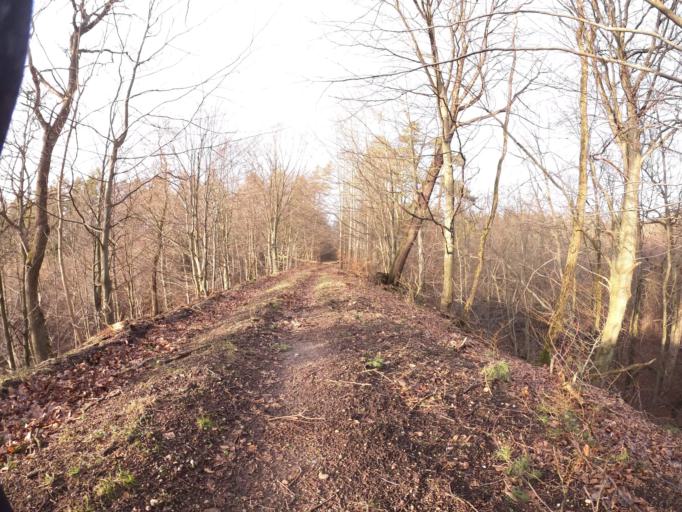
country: PL
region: West Pomeranian Voivodeship
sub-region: Powiat koszalinski
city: Polanow
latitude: 54.1797
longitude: 16.7303
